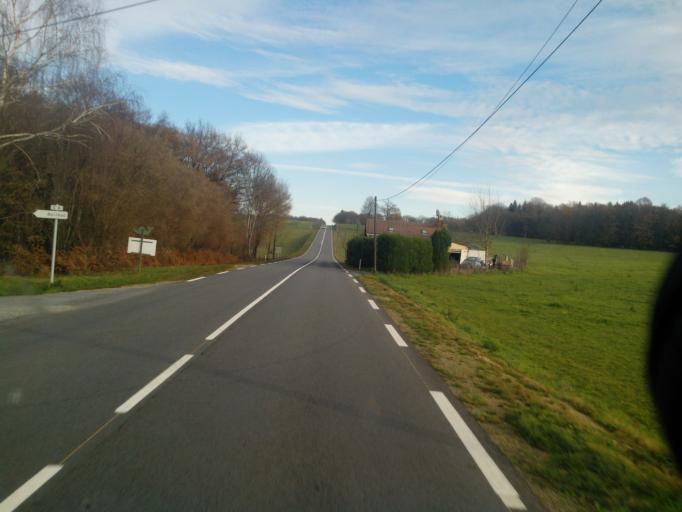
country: FR
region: Limousin
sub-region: Departement de la Haute-Vienne
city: Neuvic-Entier
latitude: 45.7303
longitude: 1.6319
